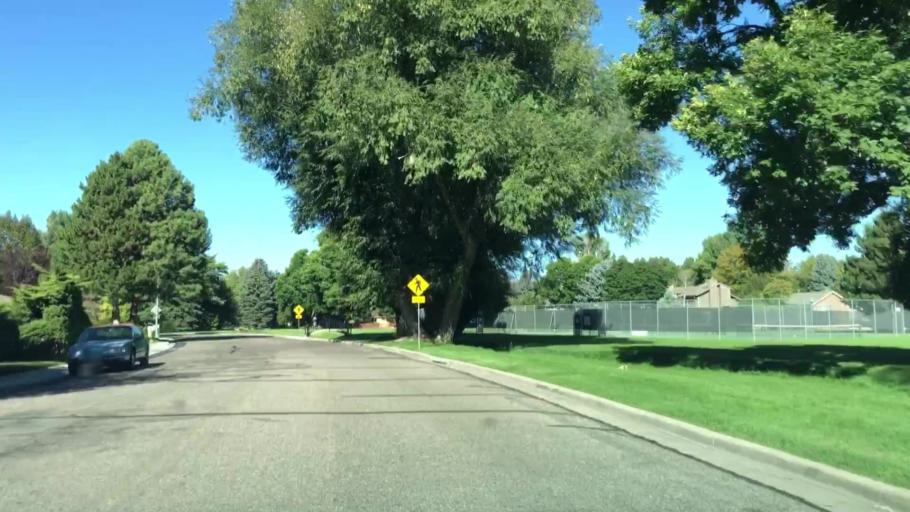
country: US
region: Colorado
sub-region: Larimer County
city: Fort Collins
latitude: 40.5582
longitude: -105.0539
